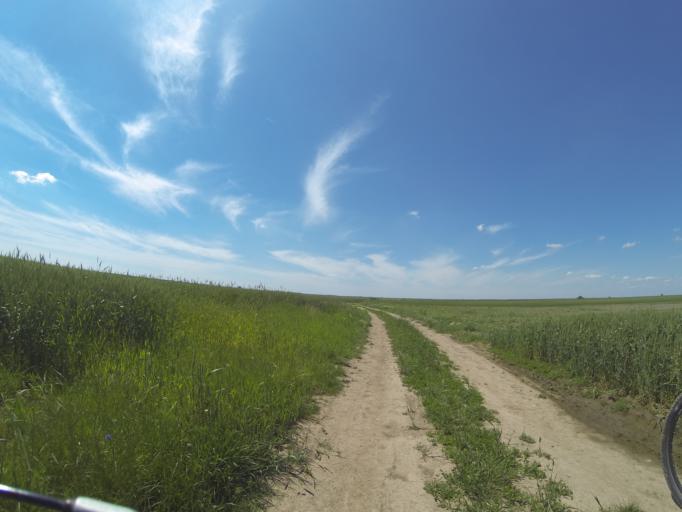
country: RO
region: Dolj
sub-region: Comuna Leu
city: Leu
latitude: 44.2216
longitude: 24.0056
